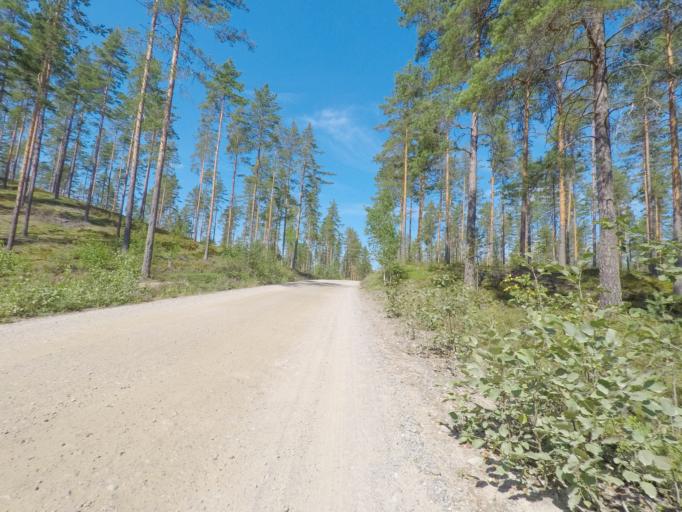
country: FI
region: Southern Savonia
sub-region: Mikkeli
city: Puumala
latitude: 61.4155
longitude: 28.0439
